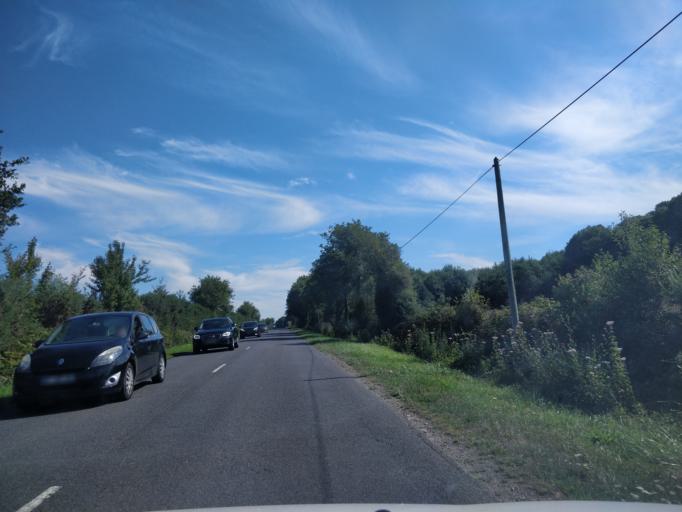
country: FR
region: Pays de la Loire
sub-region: Departement de la Loire-Atlantique
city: Quilly
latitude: 47.4862
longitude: -1.9070
